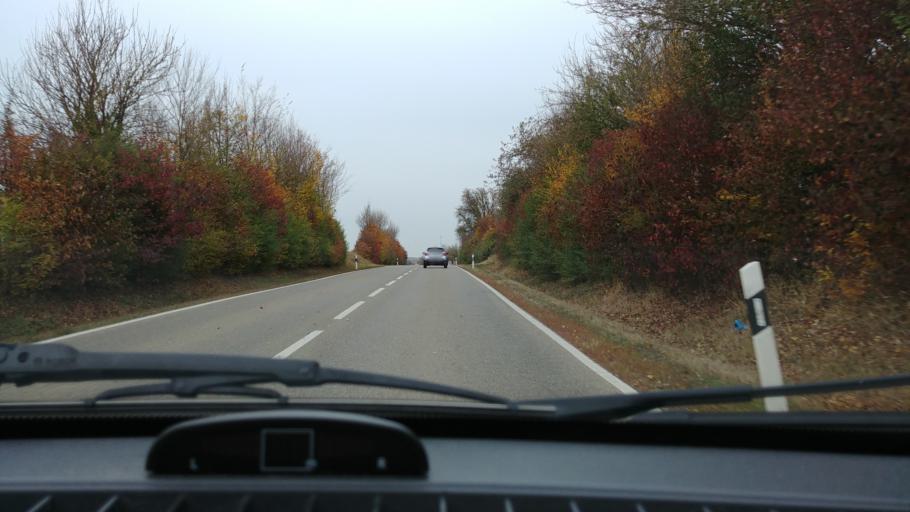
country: DE
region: Baden-Wuerttemberg
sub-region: Regierungsbezirk Stuttgart
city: Rot am See
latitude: 49.2343
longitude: 10.0420
